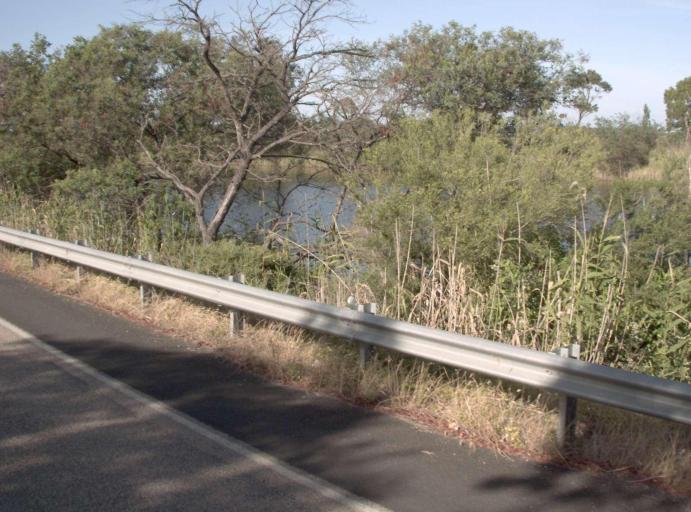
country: AU
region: Victoria
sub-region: East Gippsland
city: Lakes Entrance
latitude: -37.8339
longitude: 147.8624
